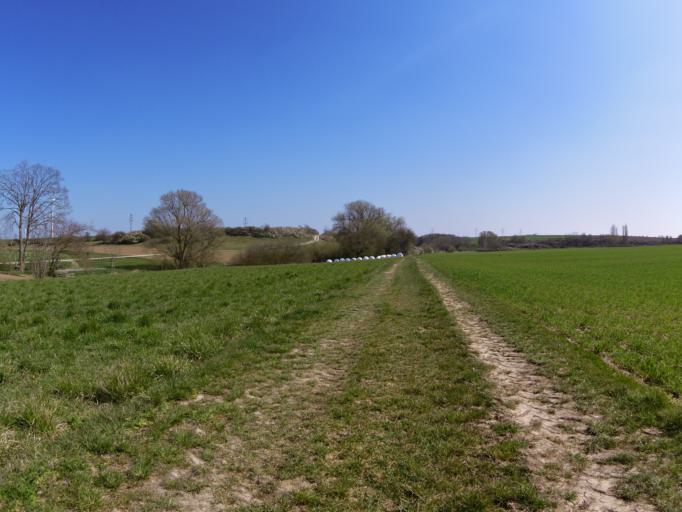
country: DE
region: Bavaria
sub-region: Regierungsbezirk Unterfranken
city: Biebelried
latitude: 49.7443
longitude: 10.0889
